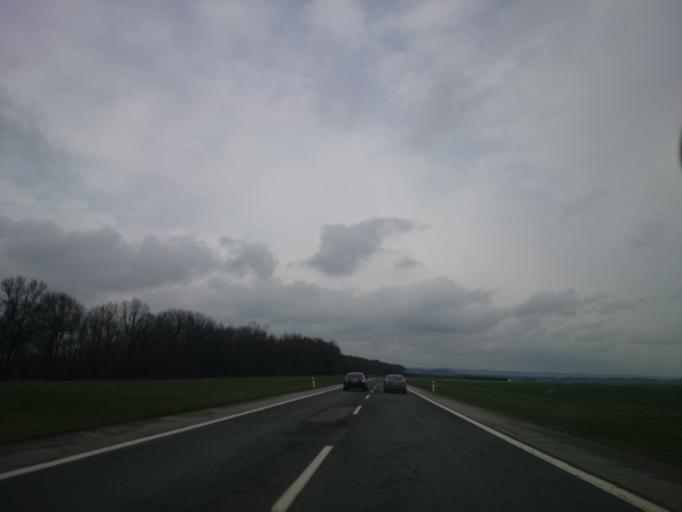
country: PL
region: Opole Voivodeship
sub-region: Powiat nyski
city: Kamienica
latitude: 50.4558
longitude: 16.9291
